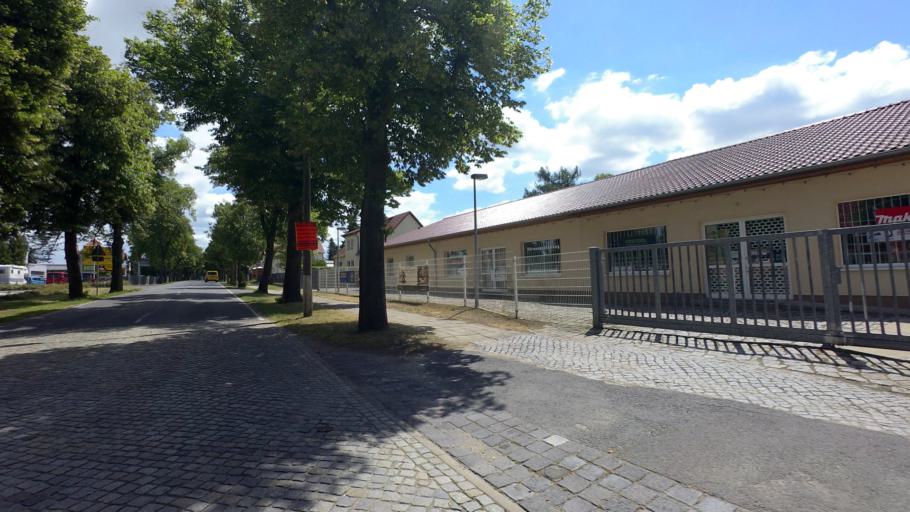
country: DE
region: Brandenburg
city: Dahme
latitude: 51.8658
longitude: 13.4372
